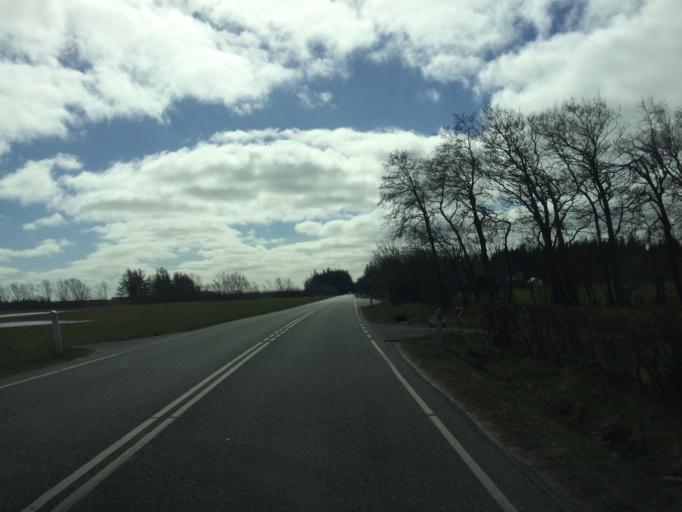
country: DK
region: Central Jutland
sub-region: Holstebro Kommune
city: Ulfborg
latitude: 56.3014
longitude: 8.1878
